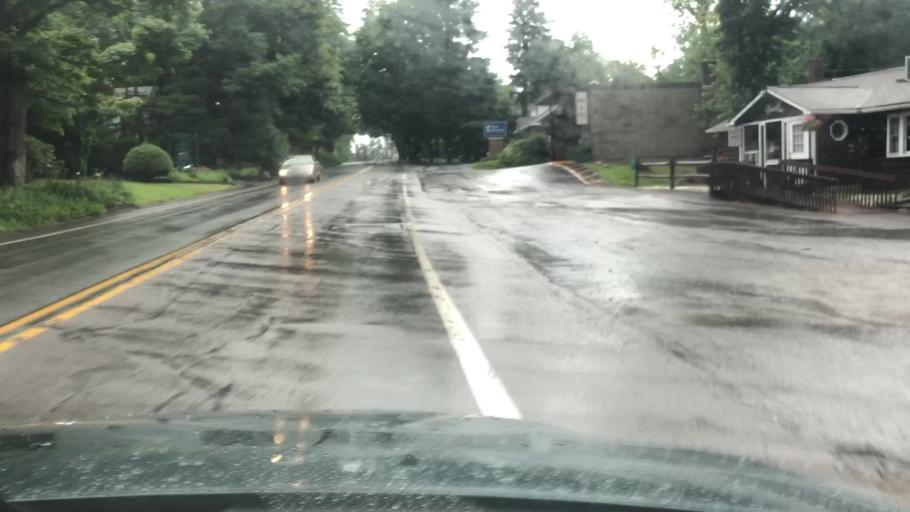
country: US
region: Pennsylvania
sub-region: Monroe County
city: Mountainhome
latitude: 41.1810
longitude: -75.2685
